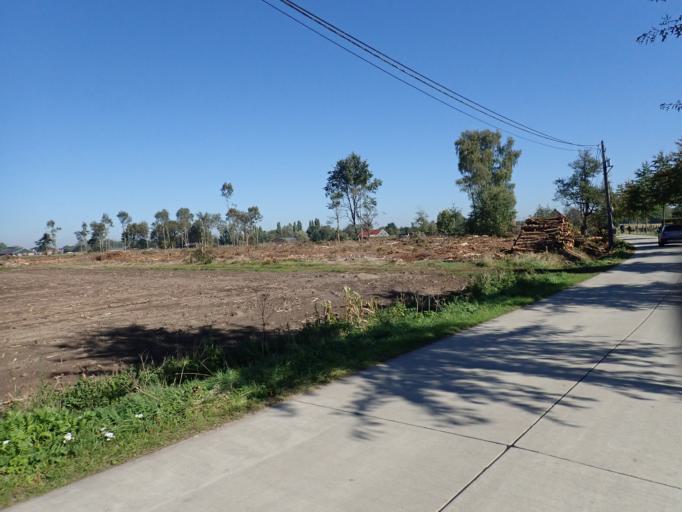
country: BE
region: Flanders
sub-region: Provincie Antwerpen
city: Rijkevorsel
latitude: 51.3712
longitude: 4.7657
